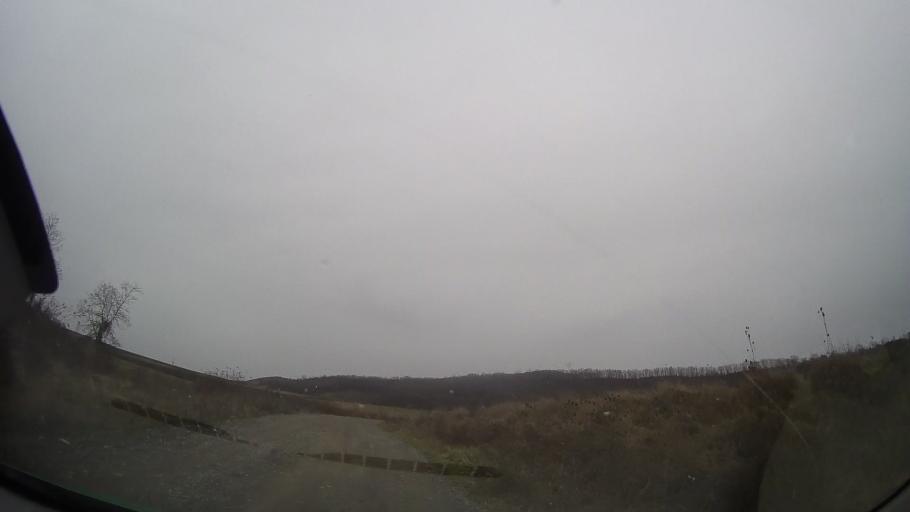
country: RO
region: Mures
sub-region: Comuna Ceausu de Campie
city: Ceausu de Campie
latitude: 46.6483
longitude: 24.4975
